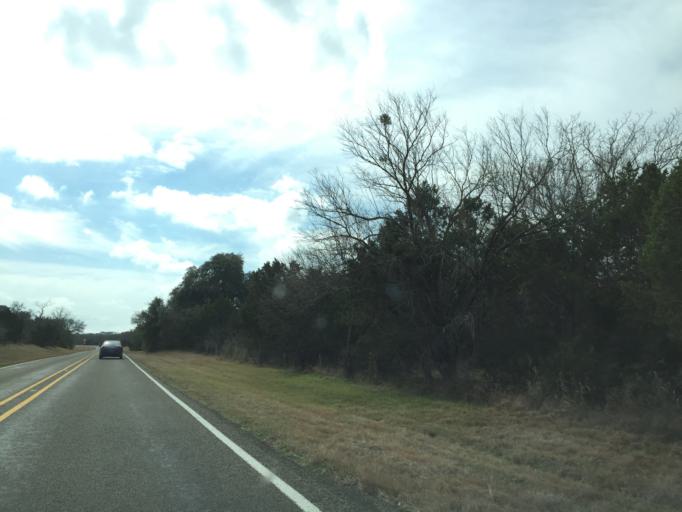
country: US
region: Texas
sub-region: Burnet County
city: Granite Shoals
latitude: 30.5091
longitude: -98.4402
